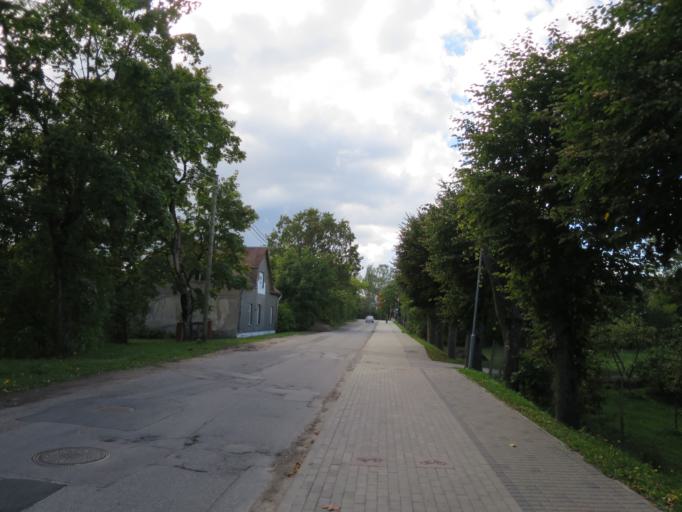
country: LV
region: Sigulda
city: Sigulda
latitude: 57.1545
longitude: 24.8489
